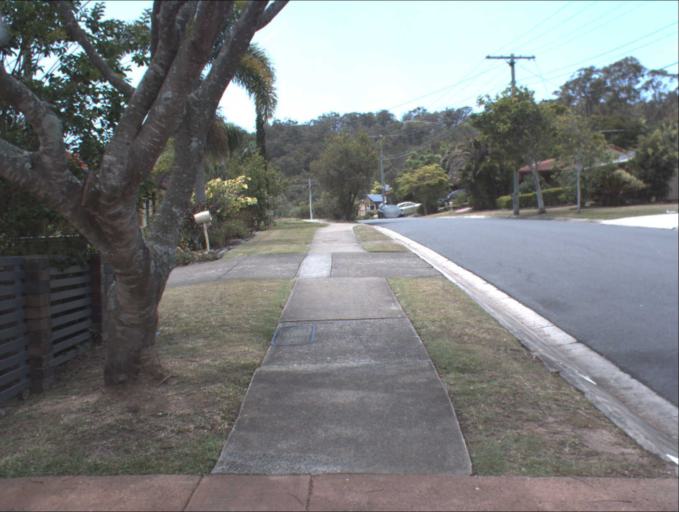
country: AU
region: Queensland
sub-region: Logan
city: Springwood
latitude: -27.6247
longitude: 153.1380
